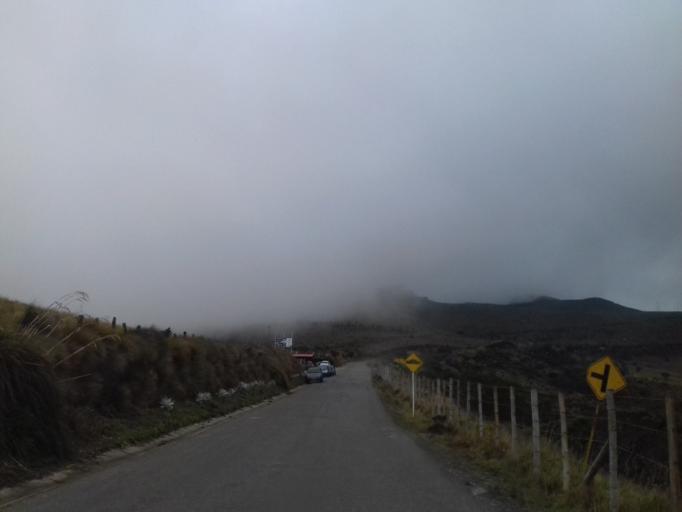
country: CO
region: Caldas
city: Villamaria
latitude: 4.9815
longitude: -75.3352
